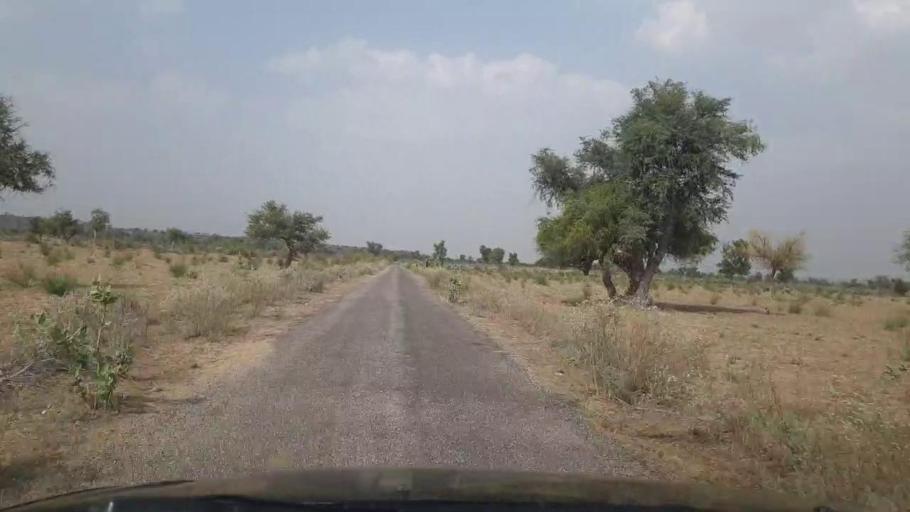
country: PK
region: Sindh
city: Islamkot
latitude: 24.9051
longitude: 70.5586
